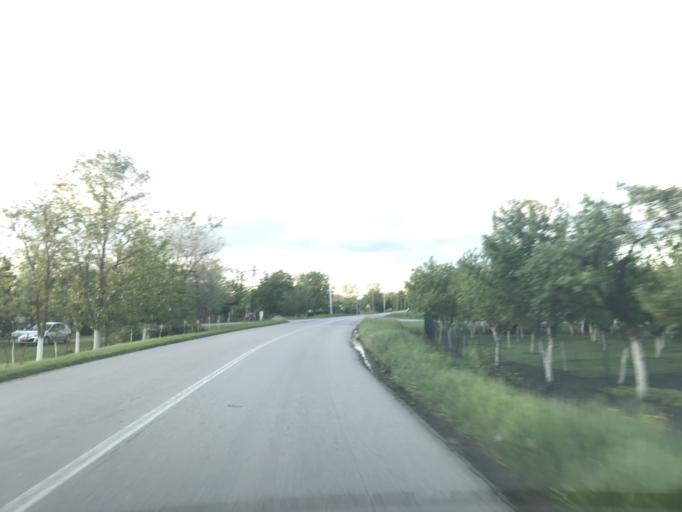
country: RS
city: Cestereg
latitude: 45.5574
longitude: 20.5239
